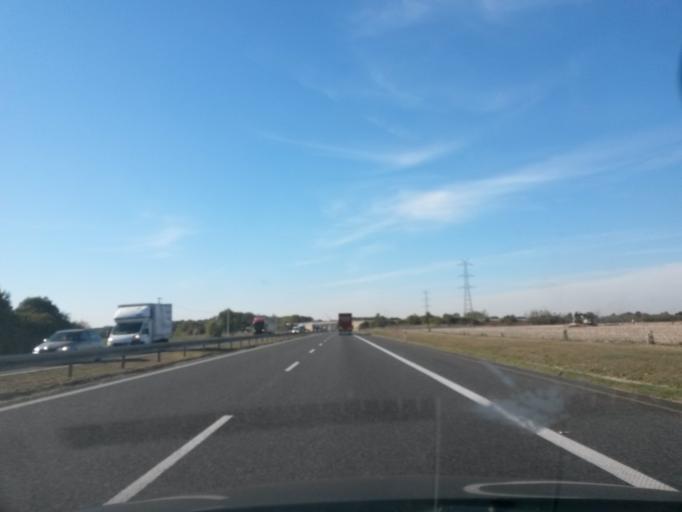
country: PL
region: Opole Voivodeship
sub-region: Powiat brzeski
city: Olszanka
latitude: 50.7612
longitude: 17.4215
